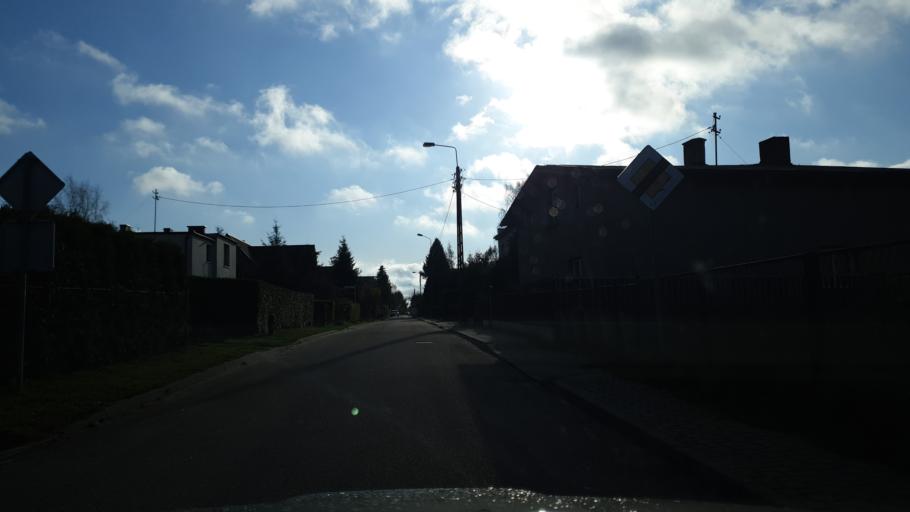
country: PL
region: Pomeranian Voivodeship
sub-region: Powiat pucki
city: Jastrzebia Gora
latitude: 54.8252
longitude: 18.2486
